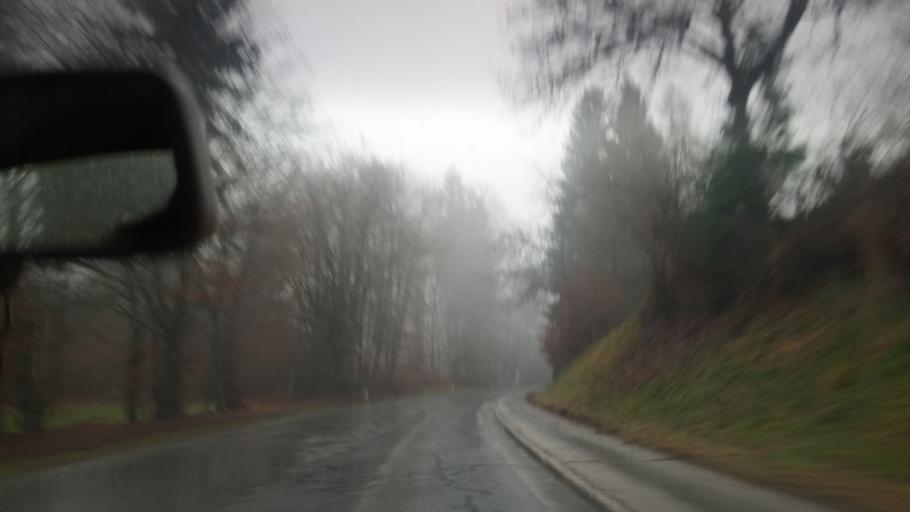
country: AT
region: Carinthia
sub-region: Politischer Bezirk Klagenfurt Land
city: Keutschach am See
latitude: 46.5903
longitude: 14.2009
